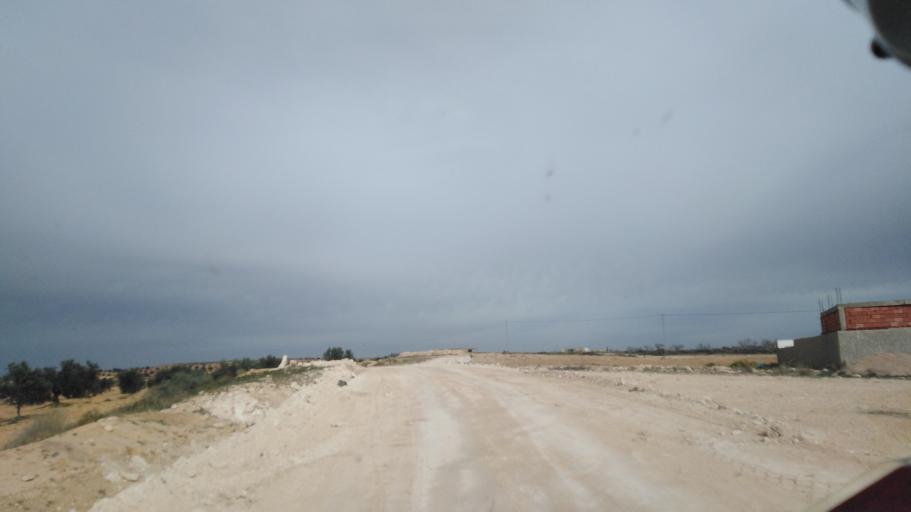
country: TN
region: Safaqis
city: Bi'r `Ali Bin Khalifah
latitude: 34.8158
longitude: 10.3072
